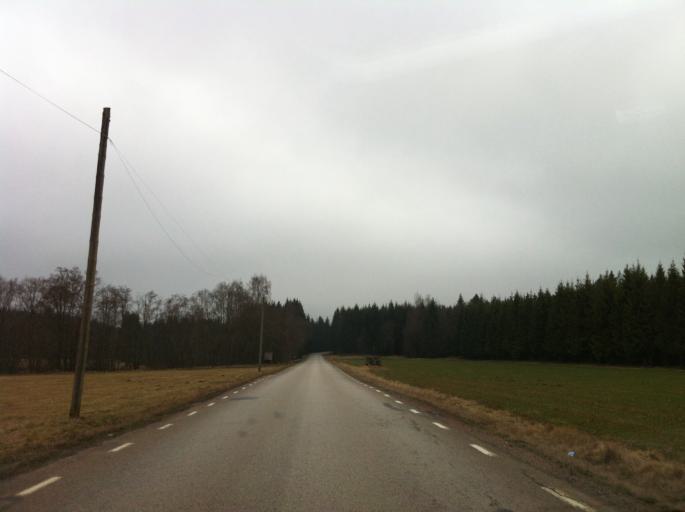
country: SE
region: Vaestra Goetaland
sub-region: Svenljunga Kommun
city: Svenljunga
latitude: 57.5220
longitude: 13.1119
